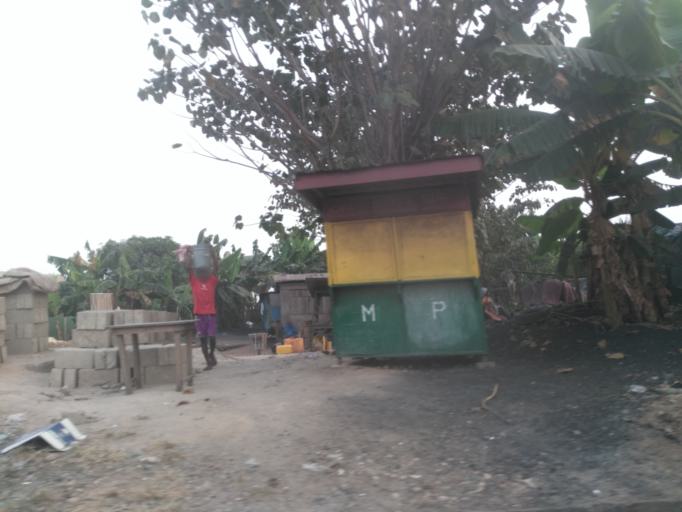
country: GH
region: Ashanti
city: Tafo
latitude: 6.7093
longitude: -1.6064
